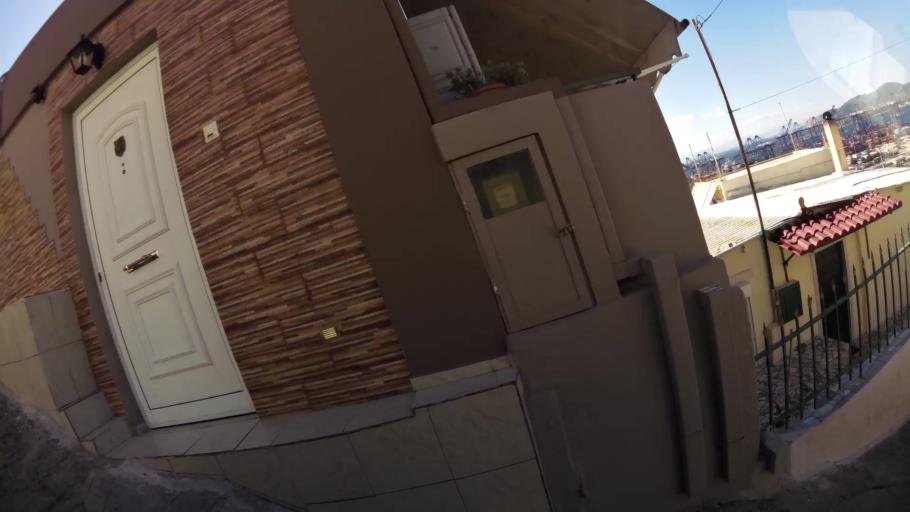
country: GR
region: Attica
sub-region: Nomos Piraios
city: Perama
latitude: 37.9647
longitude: 23.5929
